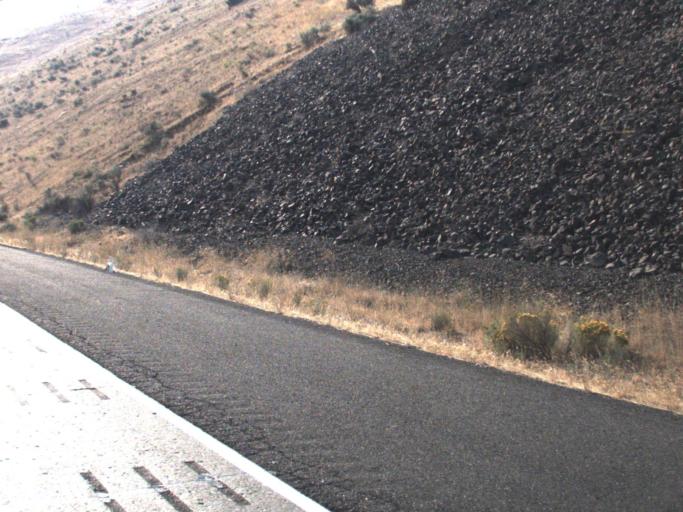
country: US
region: Washington
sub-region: Kittitas County
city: Kittitas
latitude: 46.8933
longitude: -120.4443
